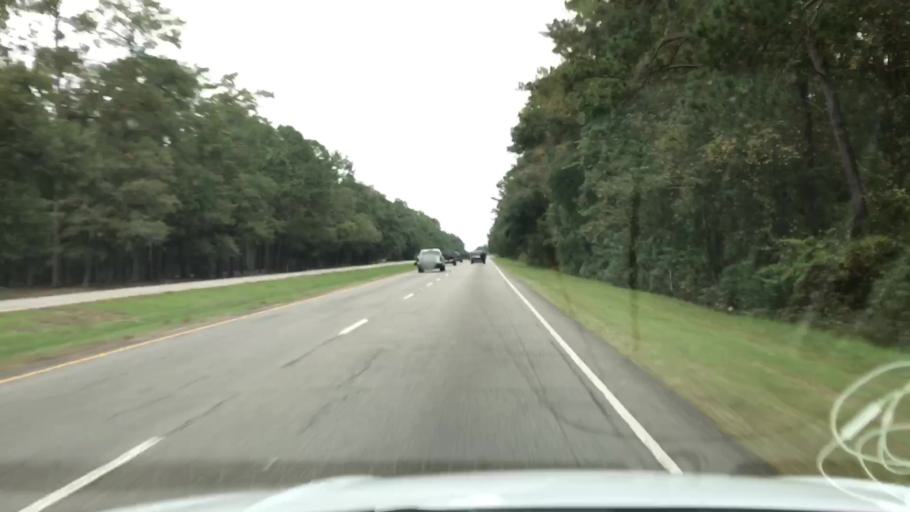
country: US
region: South Carolina
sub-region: Georgetown County
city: Murrells Inlet
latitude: 33.5180
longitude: -79.0701
